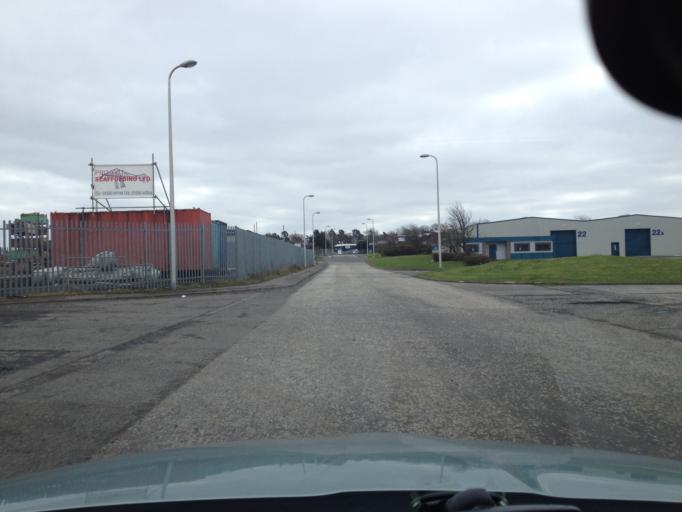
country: GB
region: Scotland
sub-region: West Lothian
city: Livingston
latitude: 55.9074
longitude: -3.5008
